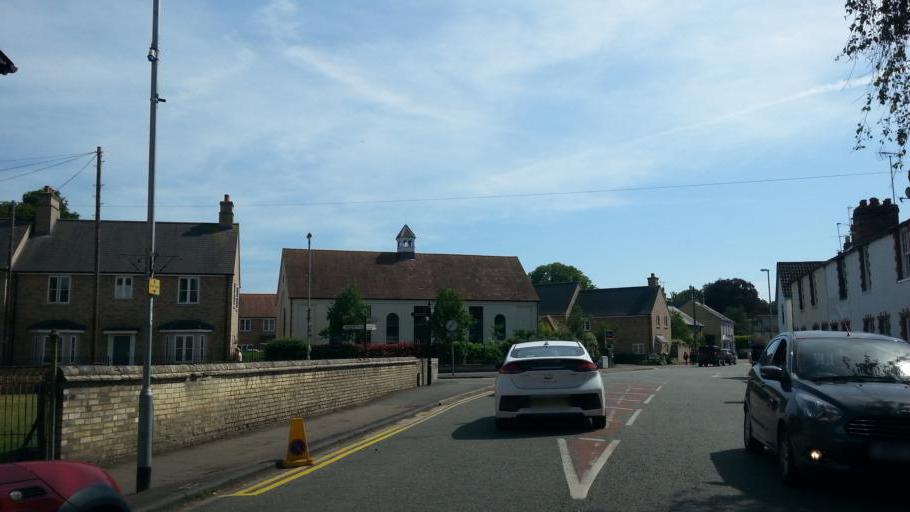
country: GB
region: England
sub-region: Cambridgeshire
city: Sawston
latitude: 52.1469
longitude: 0.1329
